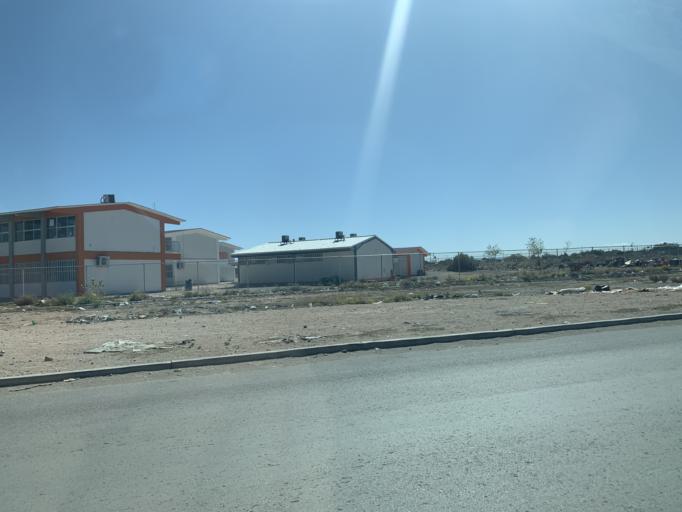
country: US
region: Texas
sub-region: El Paso County
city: Socorro Mission Number 1 Colonia
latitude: 31.5911
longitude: -106.3532
